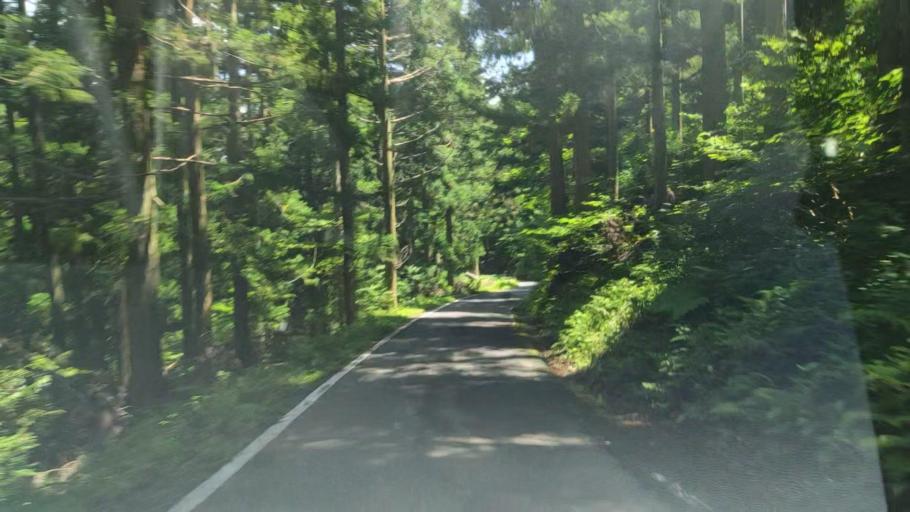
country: JP
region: Fukui
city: Ono
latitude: 35.7630
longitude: 136.5544
